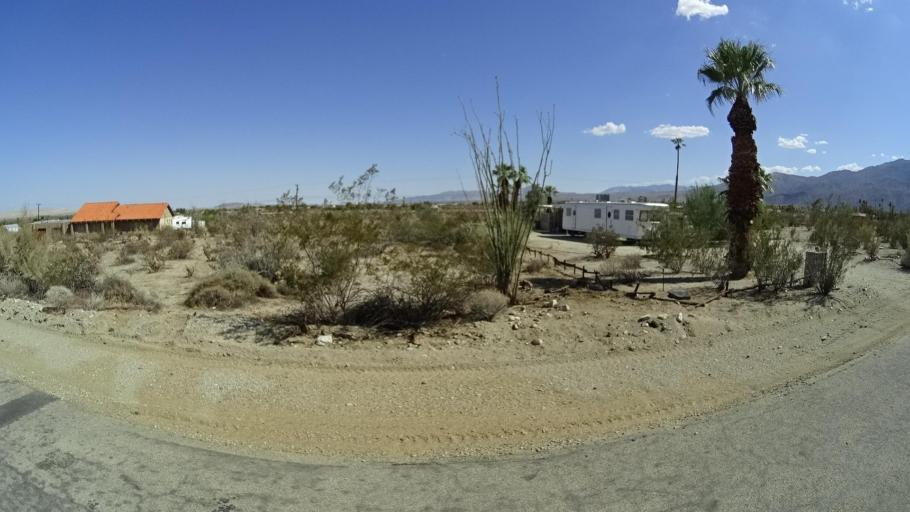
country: US
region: California
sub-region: San Diego County
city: Borrego Springs
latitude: 33.2414
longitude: -116.3811
